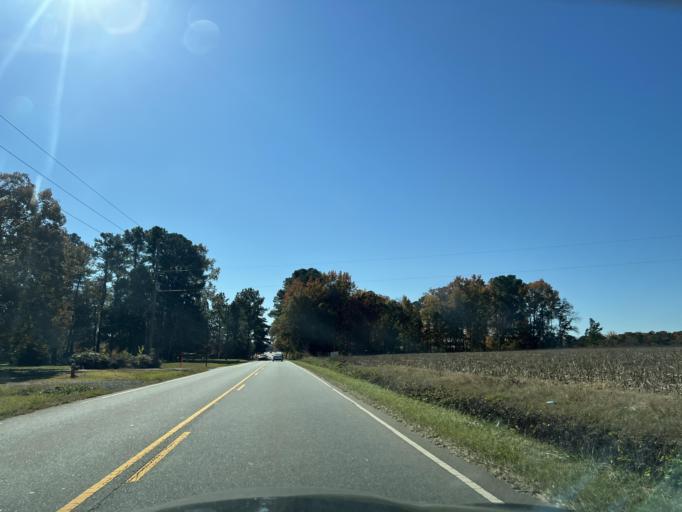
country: US
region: North Carolina
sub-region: Wake County
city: Fuquay-Varina
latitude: 35.6539
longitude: -78.7190
